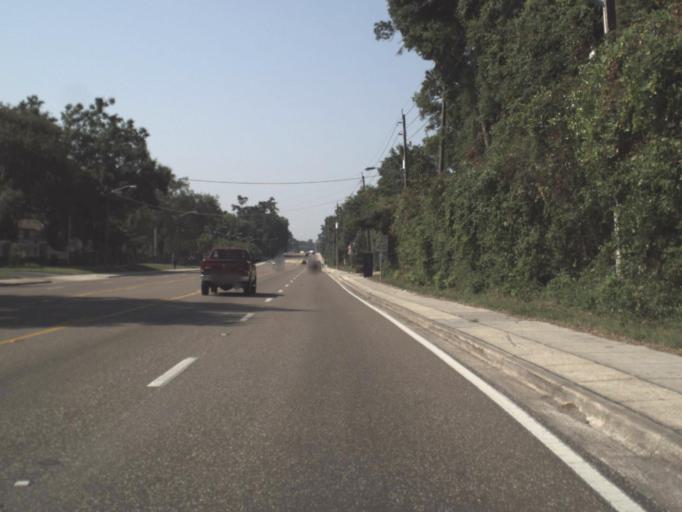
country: US
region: Florida
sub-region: Duval County
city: Jacksonville
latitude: 30.2917
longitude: -81.7554
